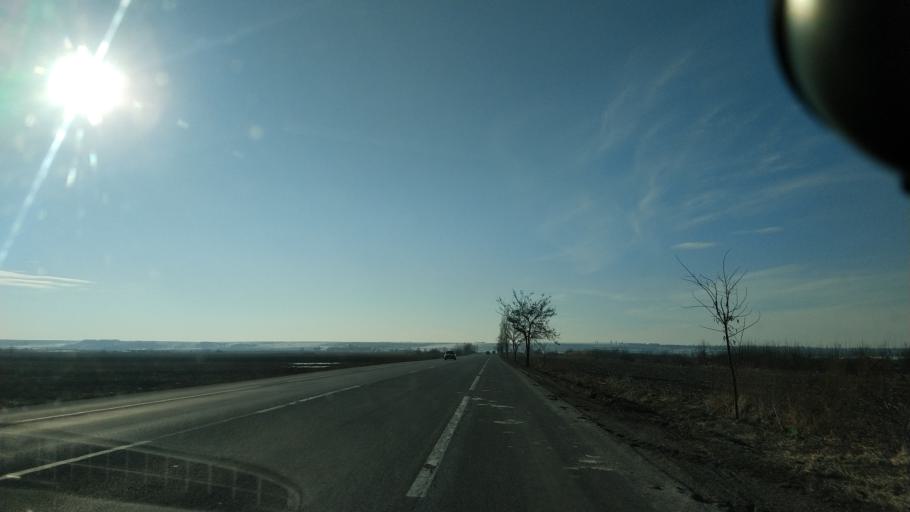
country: RO
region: Iasi
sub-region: Comuna Butea
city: Butea
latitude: 47.0745
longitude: 26.8923
